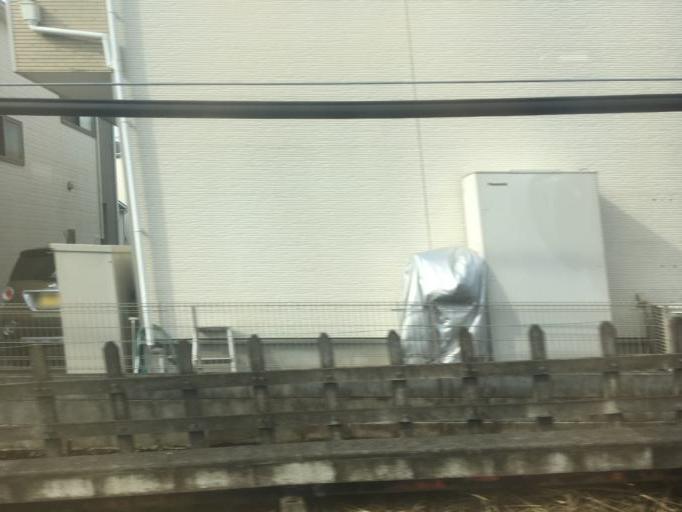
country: JP
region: Saitama
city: Sayama
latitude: 35.8307
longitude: 139.4104
